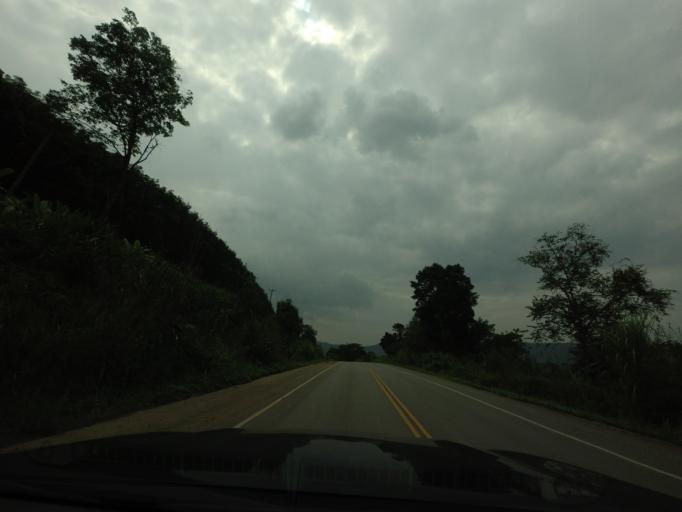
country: TH
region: Loei
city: Dan Sai
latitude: 17.2163
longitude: 101.1746
